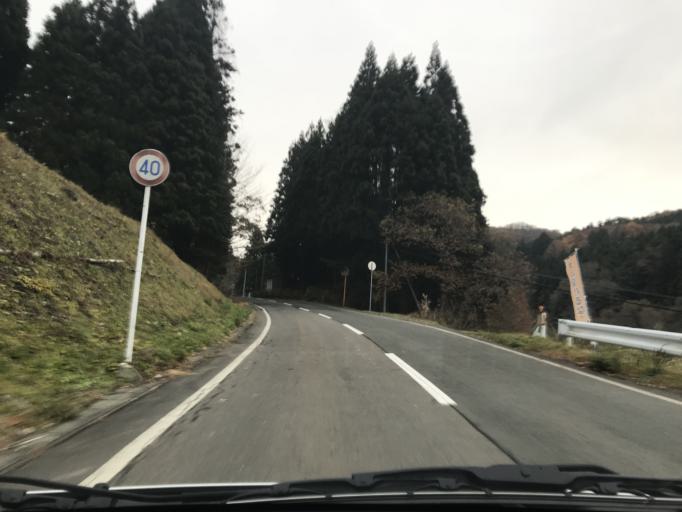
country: JP
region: Iwate
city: Tono
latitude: 39.1899
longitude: 141.3520
